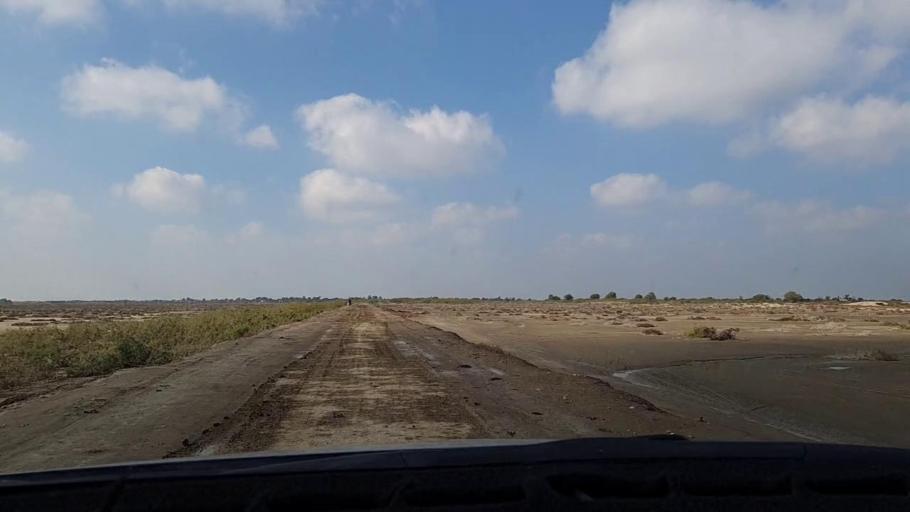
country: PK
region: Sindh
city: Tando Mittha Khan
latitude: 25.7674
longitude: 69.2672
